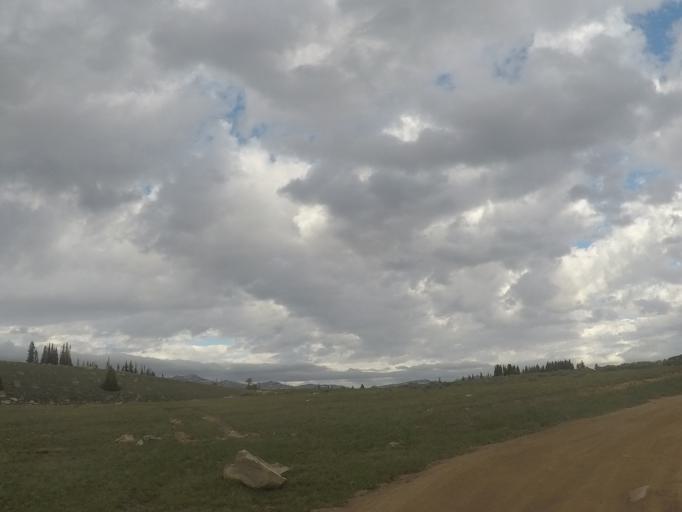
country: US
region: Wyoming
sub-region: Sheridan County
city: Sheridan
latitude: 44.5038
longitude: -107.4340
